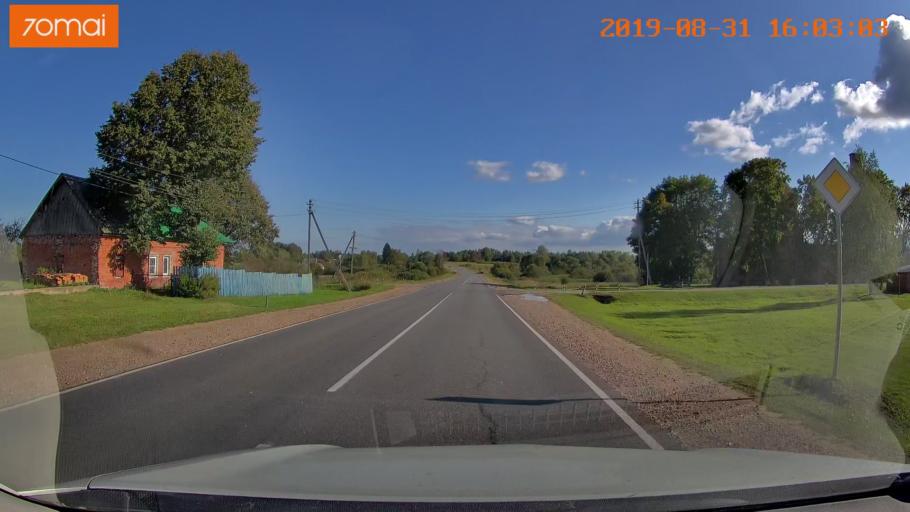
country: RU
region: Kaluga
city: Yukhnov
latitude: 54.6688
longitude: 35.3093
